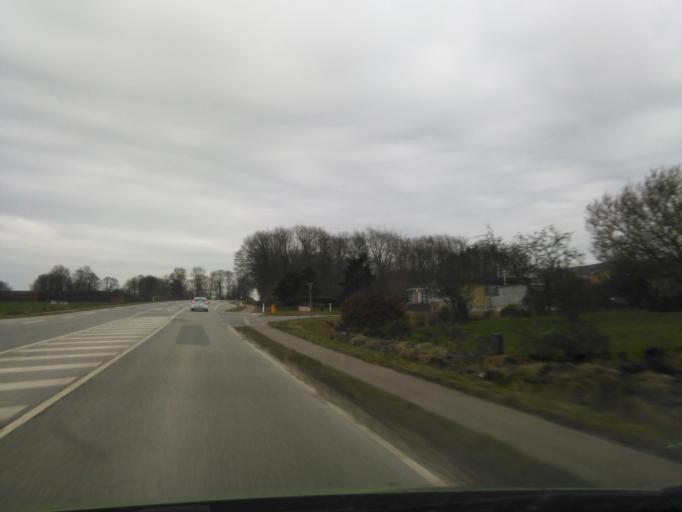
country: DK
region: Central Jutland
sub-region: Randers Kommune
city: Spentrup
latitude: 56.5034
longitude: 10.0228
